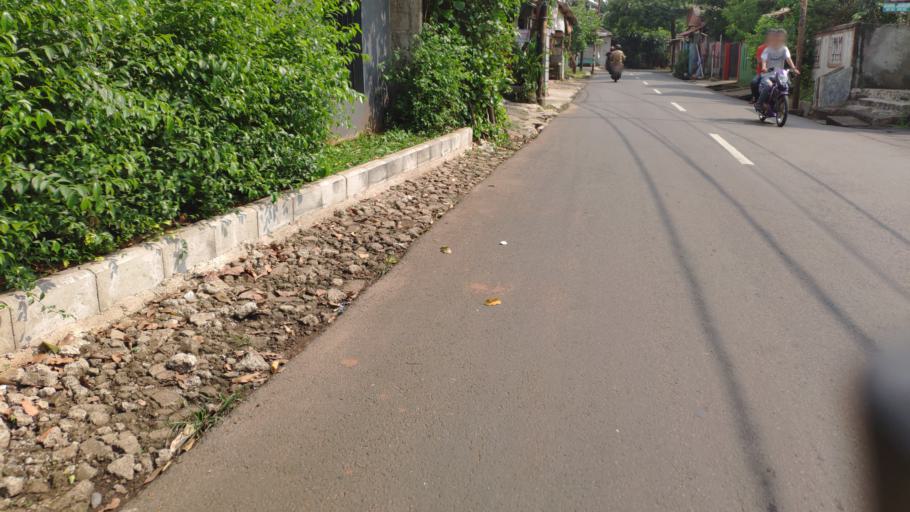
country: ID
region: West Java
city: Depok
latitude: -6.3195
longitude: 106.8187
